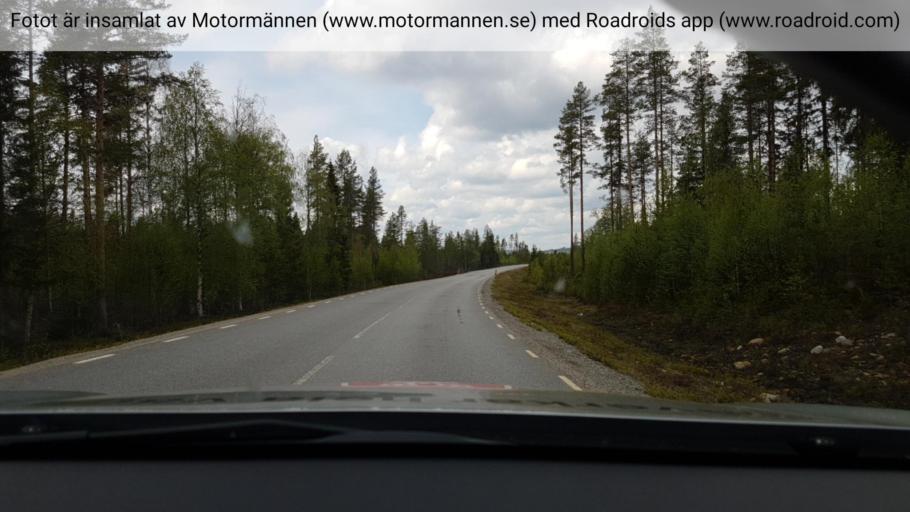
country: SE
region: Vaesternorrland
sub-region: OErnskoeldsviks Kommun
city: Ornskoldsvik
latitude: 63.8773
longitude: 18.5497
